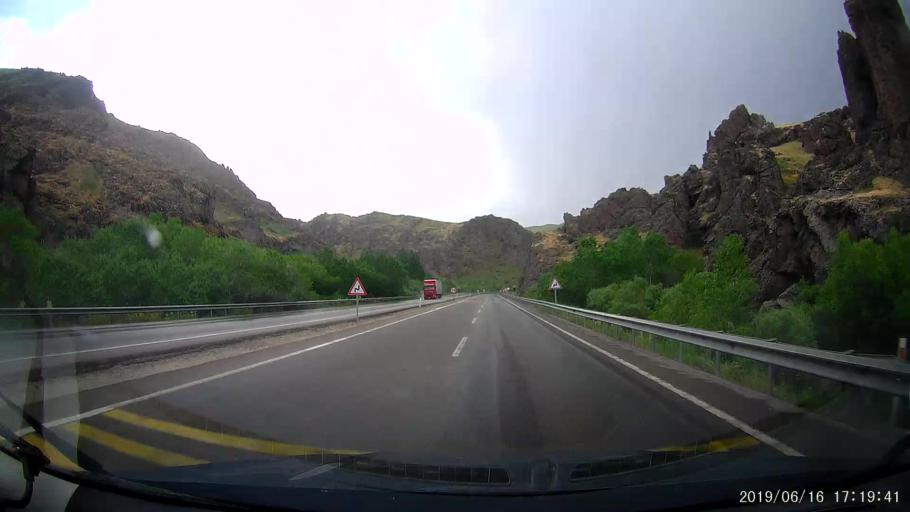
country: TR
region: Erzincan
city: Tercan
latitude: 39.8008
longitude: 40.5252
